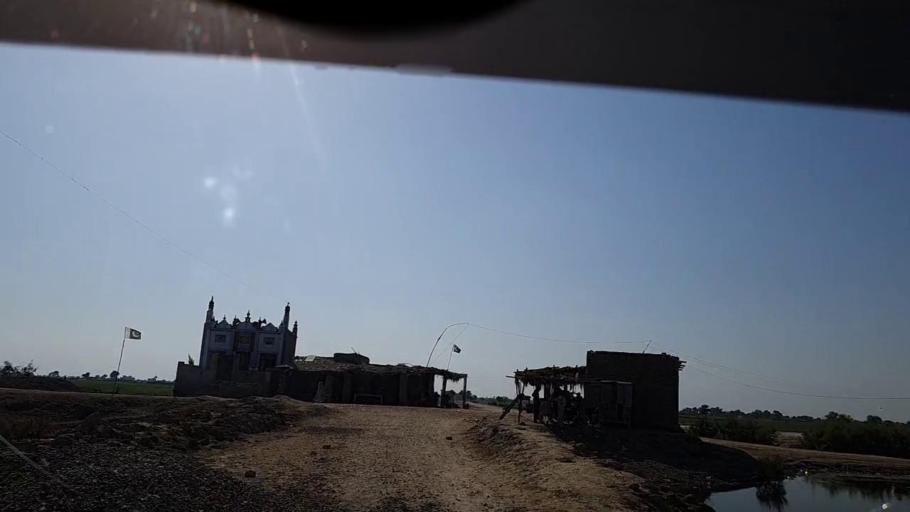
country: PK
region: Sindh
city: Tangwani
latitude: 28.3621
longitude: 69.0138
